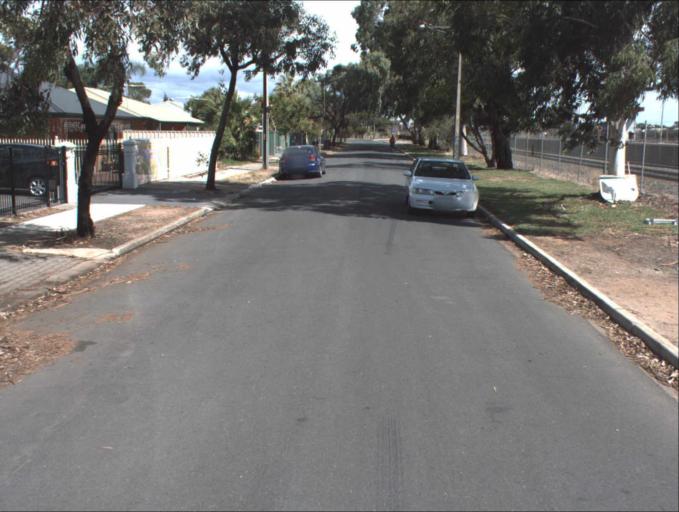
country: AU
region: South Australia
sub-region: Port Adelaide Enfield
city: Blair Athol
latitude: -34.8584
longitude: 138.5784
